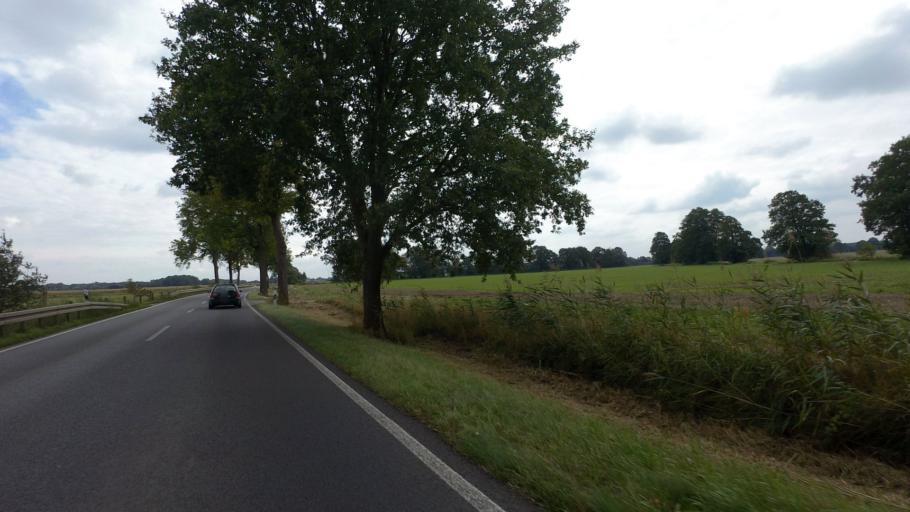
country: DE
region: Brandenburg
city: Golssen
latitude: 51.9612
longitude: 13.6244
